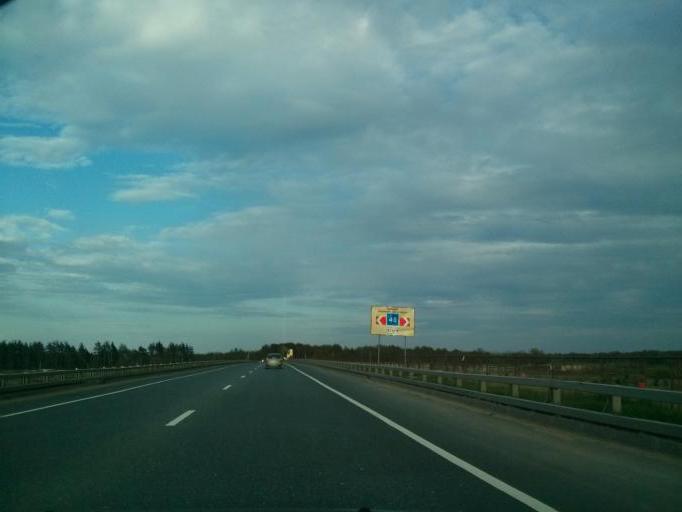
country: RU
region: Nizjnij Novgorod
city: Navashino
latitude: 55.5867
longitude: 42.1418
